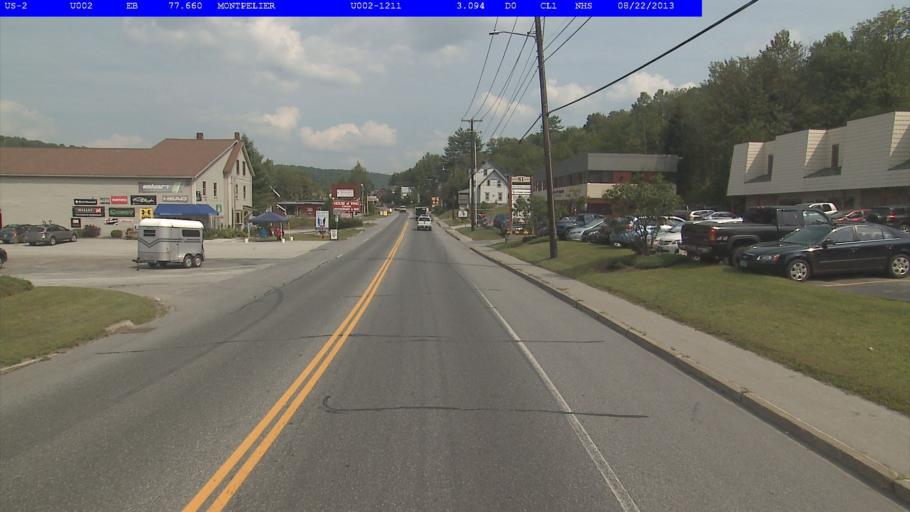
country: US
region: Vermont
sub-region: Washington County
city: Montpelier
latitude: 44.2489
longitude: -72.5643
